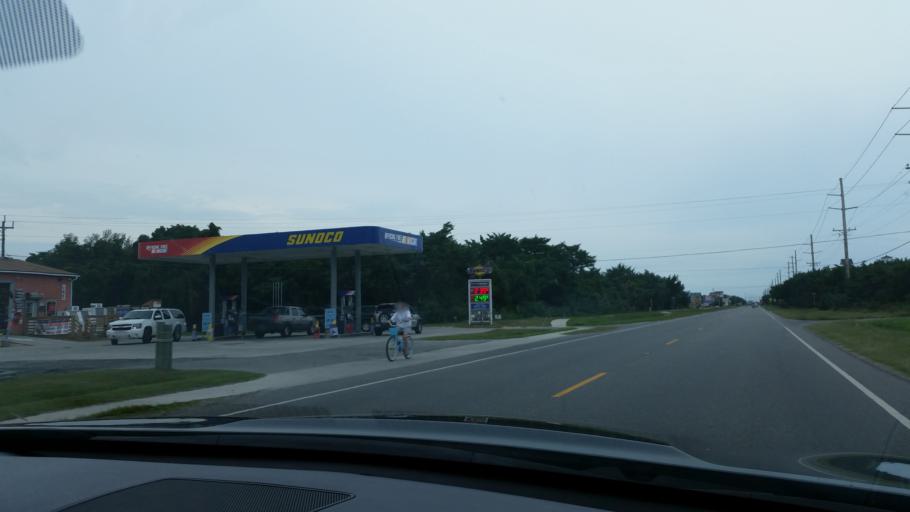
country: US
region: North Carolina
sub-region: Dare County
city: Buxton
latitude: 35.3558
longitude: -75.5025
